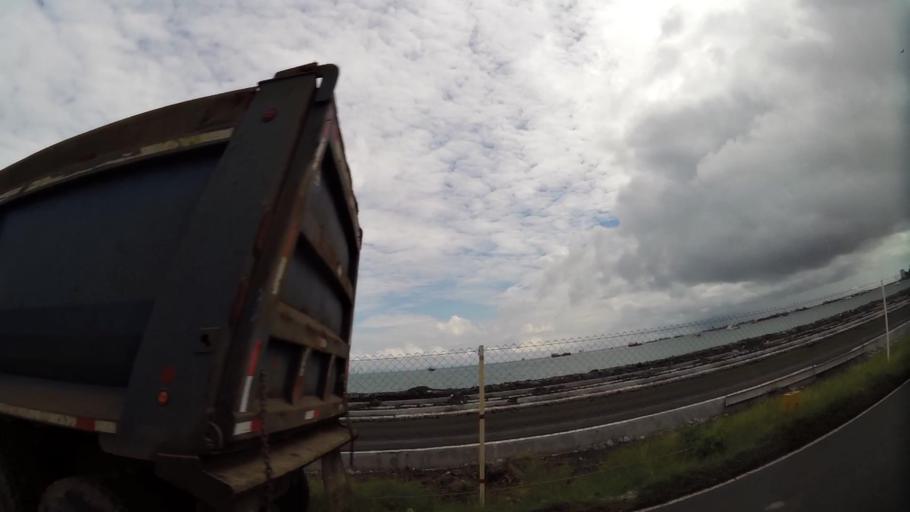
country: PA
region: Panama
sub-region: Distrito de Panama
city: Ancon
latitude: 8.9224
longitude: -79.5379
